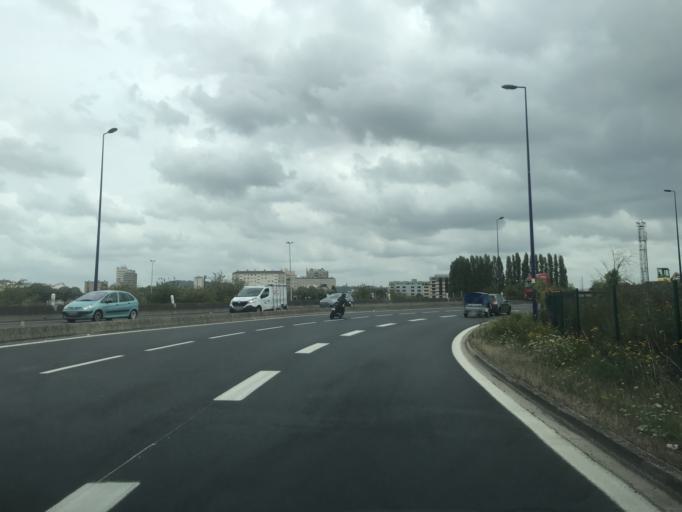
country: FR
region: Haute-Normandie
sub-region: Departement de la Seine-Maritime
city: Le Petit-Quevilly
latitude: 49.4374
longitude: 1.0714
